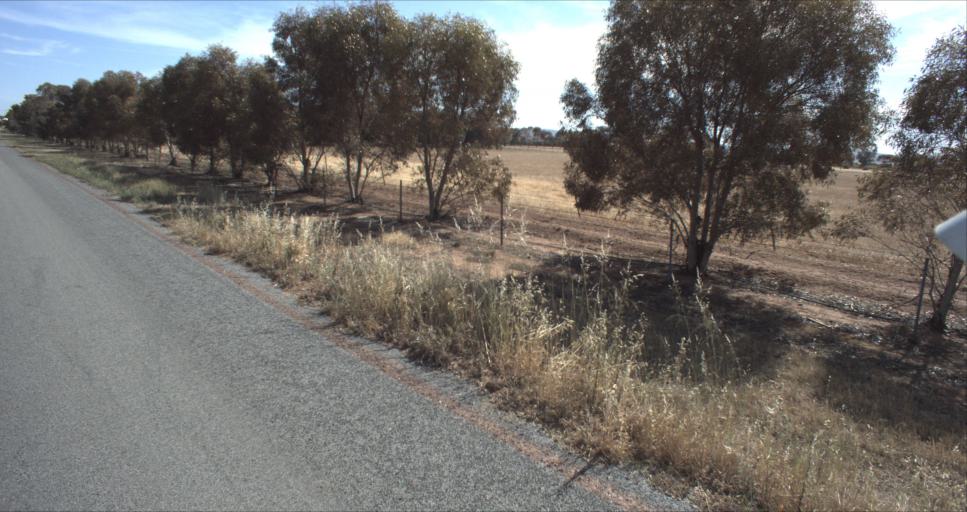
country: AU
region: New South Wales
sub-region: Leeton
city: Leeton
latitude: -34.5727
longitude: 146.4666
